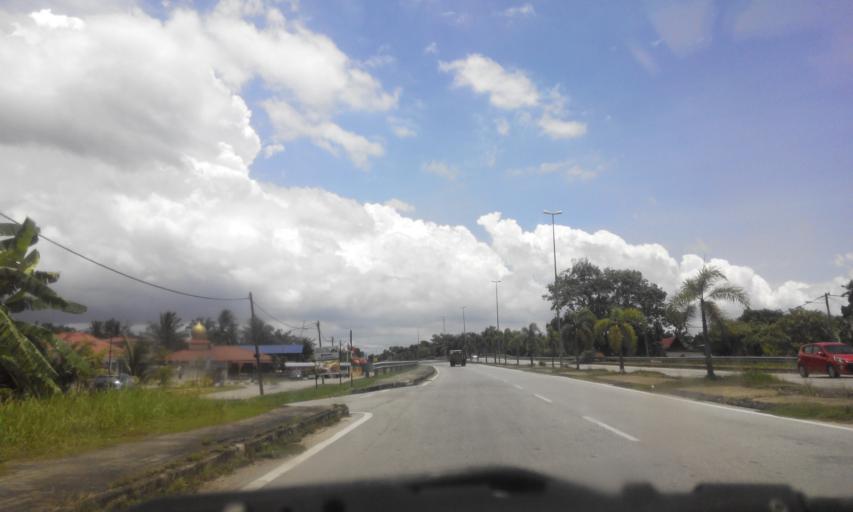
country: MY
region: Perak
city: Parit Buntar
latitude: 5.1203
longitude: 100.5209
